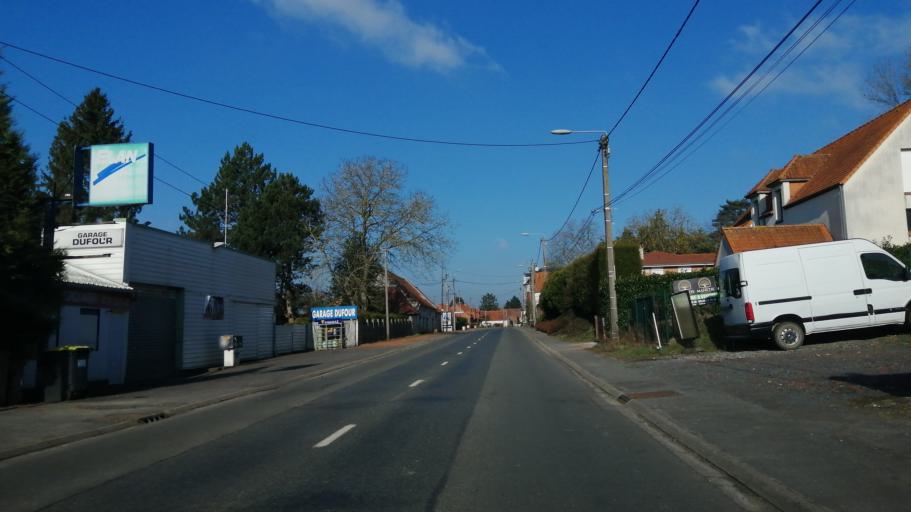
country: FR
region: Nord-Pas-de-Calais
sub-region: Departement du Pas-de-Calais
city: Mont-Saint-Eloi
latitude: 50.3704
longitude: 2.6402
